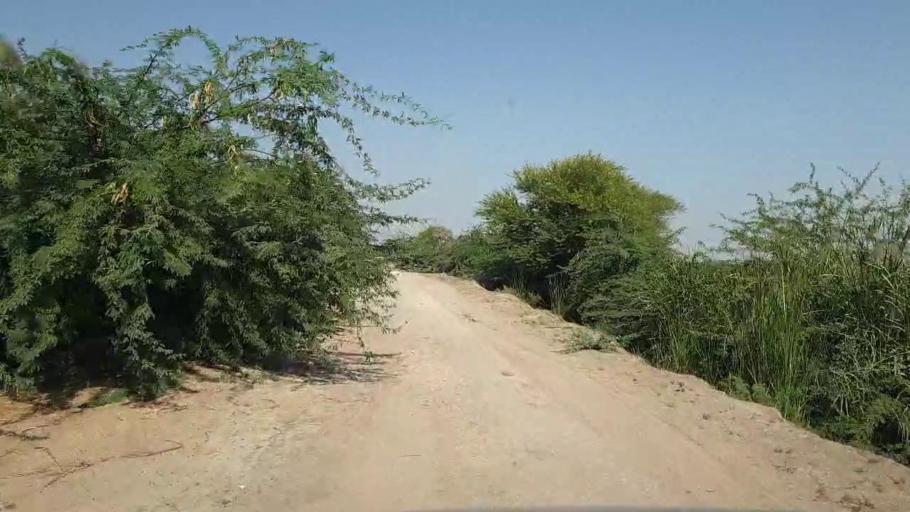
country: PK
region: Sindh
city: Tando Bago
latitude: 24.7511
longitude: 69.0283
